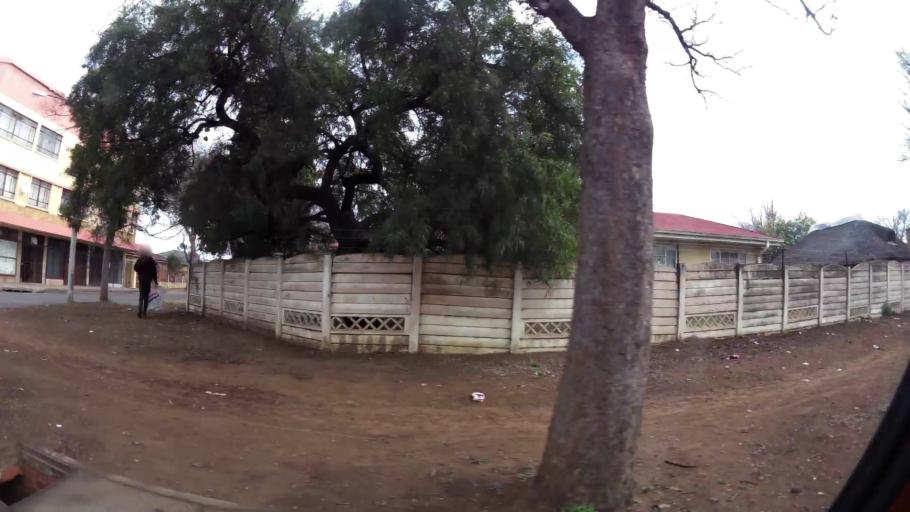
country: ZA
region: Gauteng
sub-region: Sedibeng District Municipality
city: Vanderbijlpark
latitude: -26.6915
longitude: 27.8201
